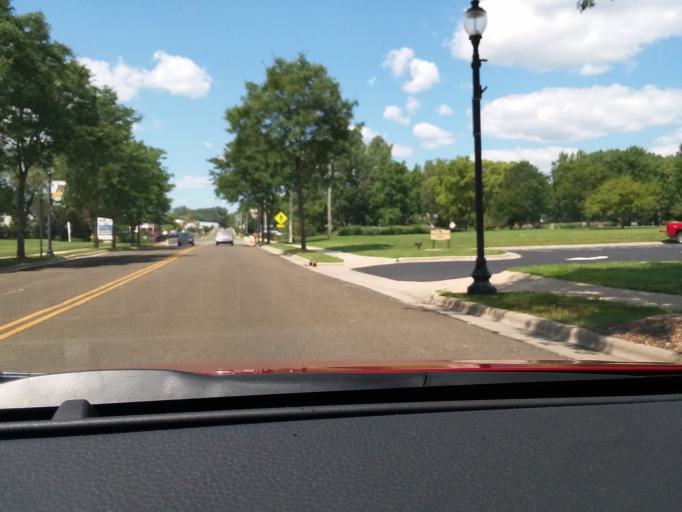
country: US
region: Wisconsin
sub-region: Dane County
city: De Forest
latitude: 43.2486
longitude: -89.3438
